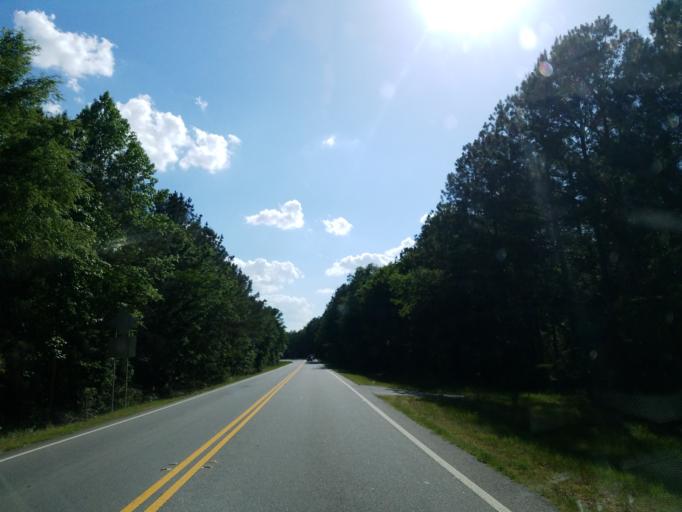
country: US
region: Georgia
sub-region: Crisp County
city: Cordele
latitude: 32.0052
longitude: -83.7404
